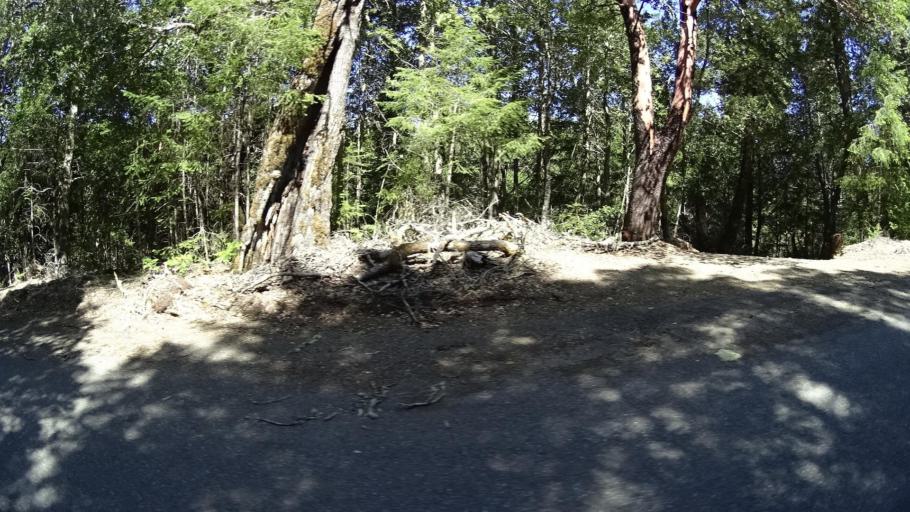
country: US
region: California
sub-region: Humboldt County
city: Redway
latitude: 40.1538
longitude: -124.0666
